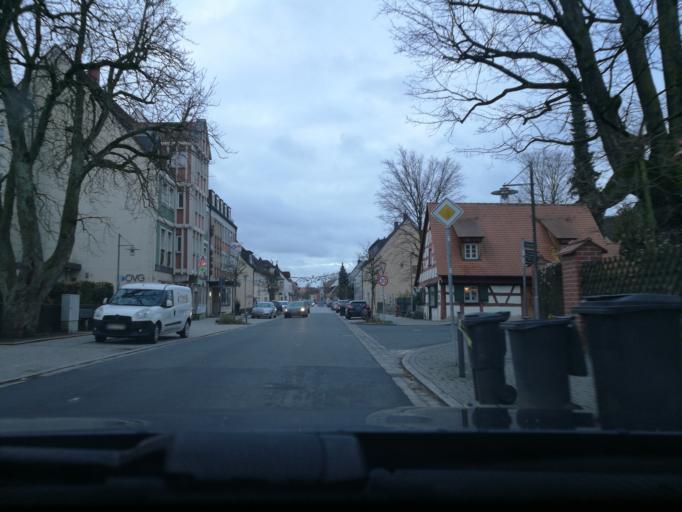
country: DE
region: Bavaria
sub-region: Regierungsbezirk Mittelfranken
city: Heroldsberg
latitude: 49.5332
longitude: 11.1526
